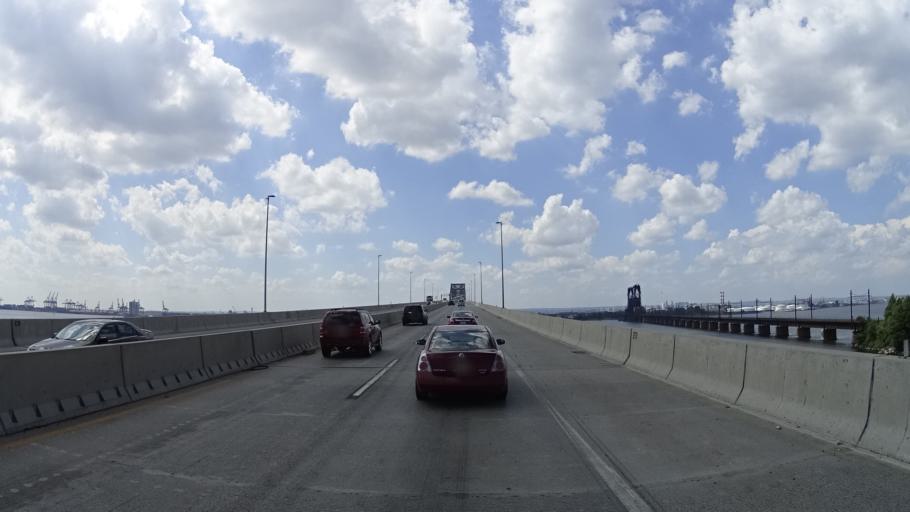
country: US
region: New Jersey
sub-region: Hudson County
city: Bayonne
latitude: 40.6926
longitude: -74.1092
